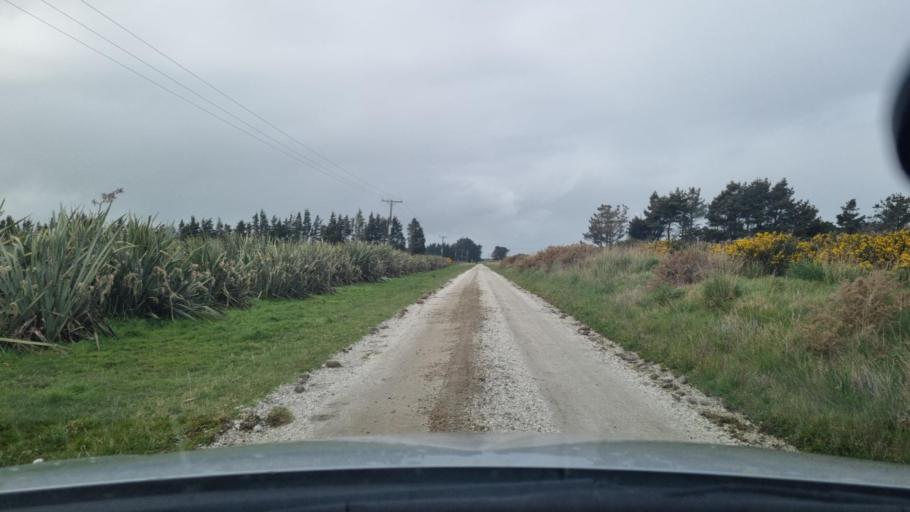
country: NZ
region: Southland
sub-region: Invercargill City
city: Invercargill
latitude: -46.4945
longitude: 168.4227
